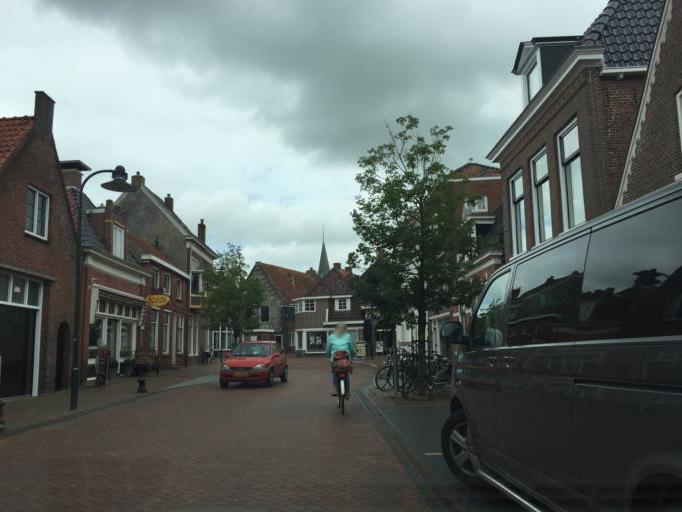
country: NL
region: Friesland
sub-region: Gemeente Dongeradeel
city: Dokkum
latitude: 53.3242
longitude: 5.9995
